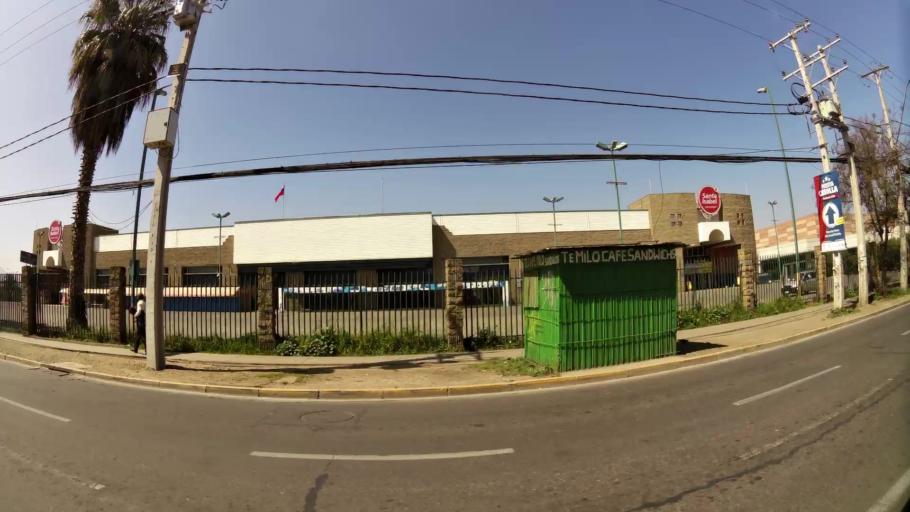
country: CL
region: Santiago Metropolitan
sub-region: Provincia de Santiago
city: Lo Prado
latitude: -33.3666
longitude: -70.7303
